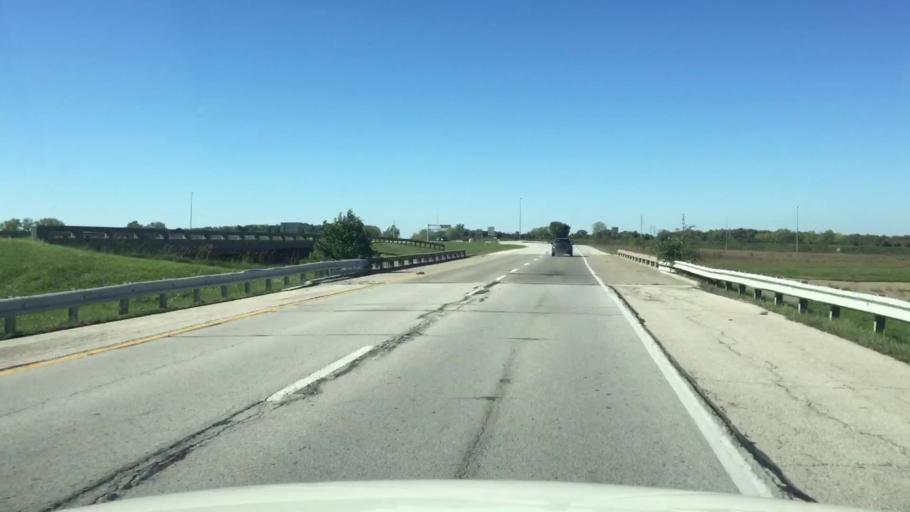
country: US
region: Kansas
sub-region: Wyandotte County
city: Edwardsville
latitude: 39.0102
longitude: -94.7793
